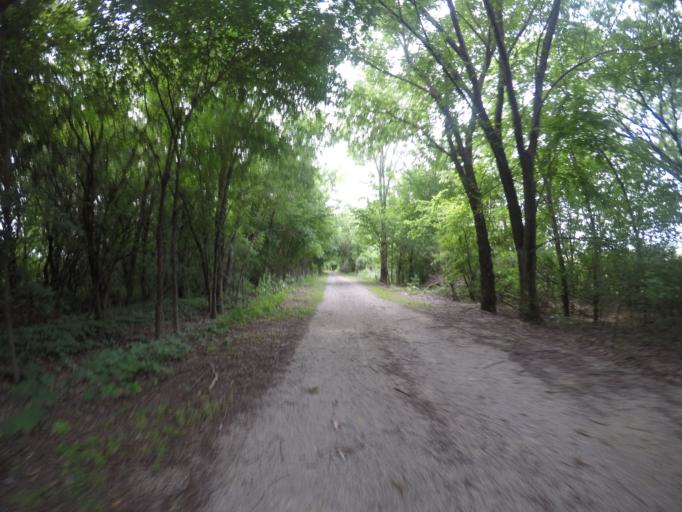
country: US
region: Kansas
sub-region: Anderson County
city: Garnett
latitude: 38.4105
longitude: -95.2612
